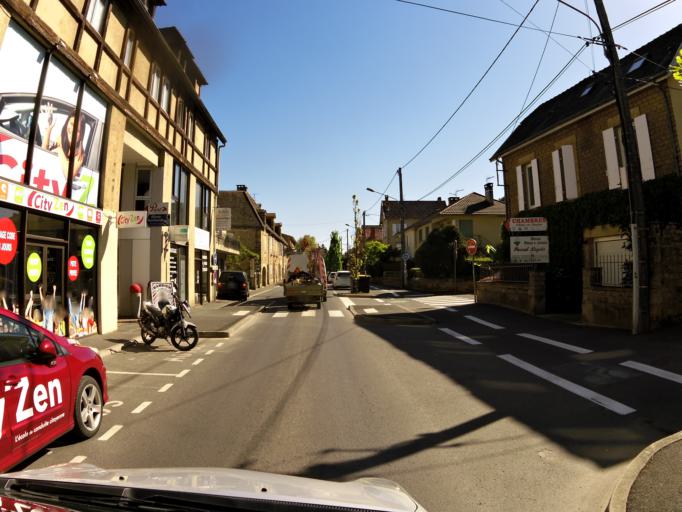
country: FR
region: Aquitaine
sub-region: Departement de la Dordogne
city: Sarlat-la-Caneda
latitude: 44.8849
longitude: 1.2163
